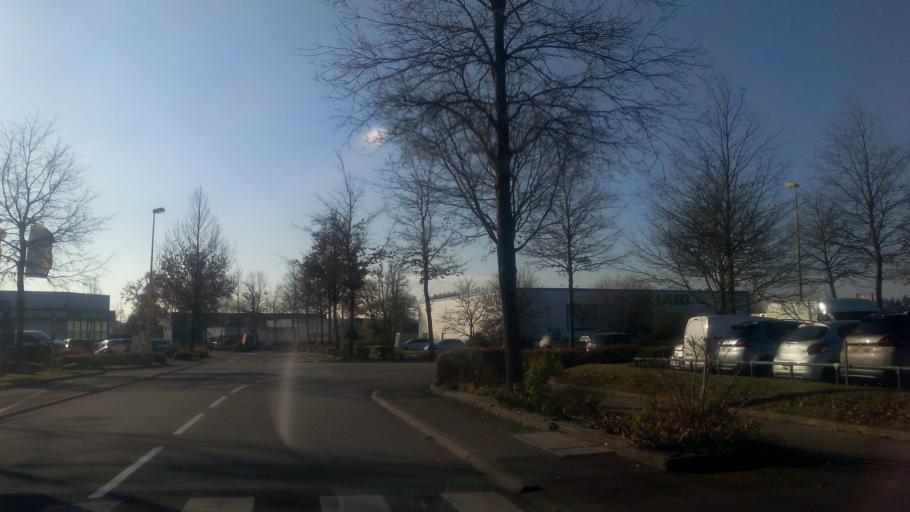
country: FR
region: Brittany
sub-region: Departement d'Ille-et-Vilaine
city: Redon
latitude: 47.6706
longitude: -2.0666
